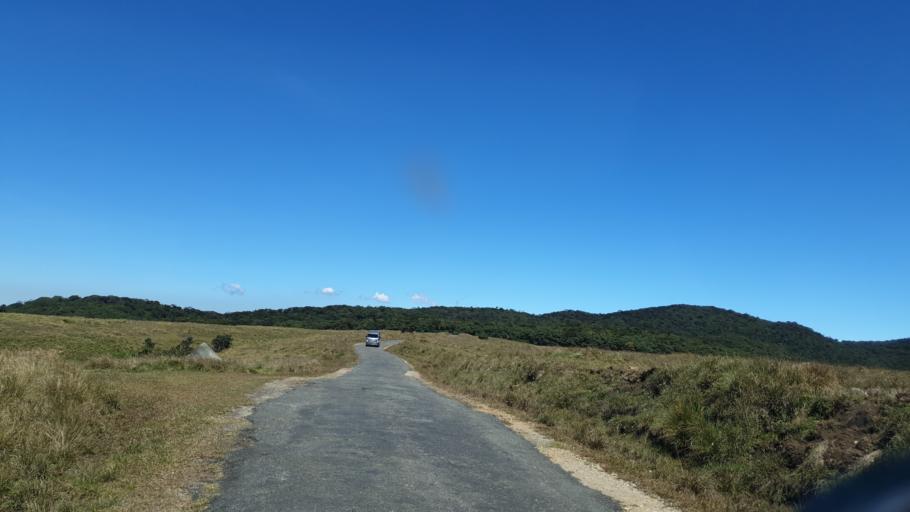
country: LK
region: Central
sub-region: Nuwara Eliya District
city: Nuwara Eliya
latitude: 6.8213
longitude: 80.8060
